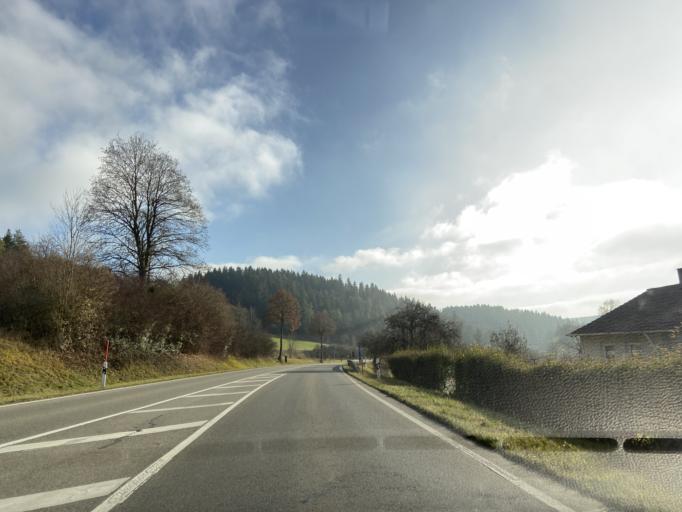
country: DE
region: Baden-Wuerttemberg
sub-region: Tuebingen Region
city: Gammertingen
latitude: 48.2446
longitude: 9.2248
